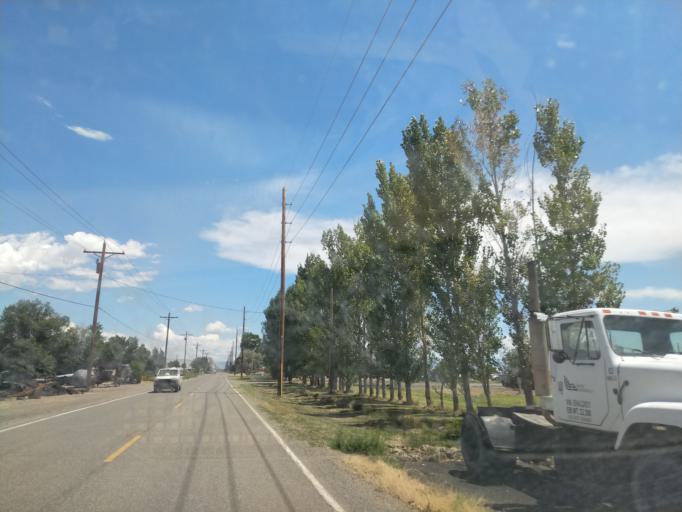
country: US
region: Colorado
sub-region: Mesa County
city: Redlands
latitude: 39.1209
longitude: -108.6592
